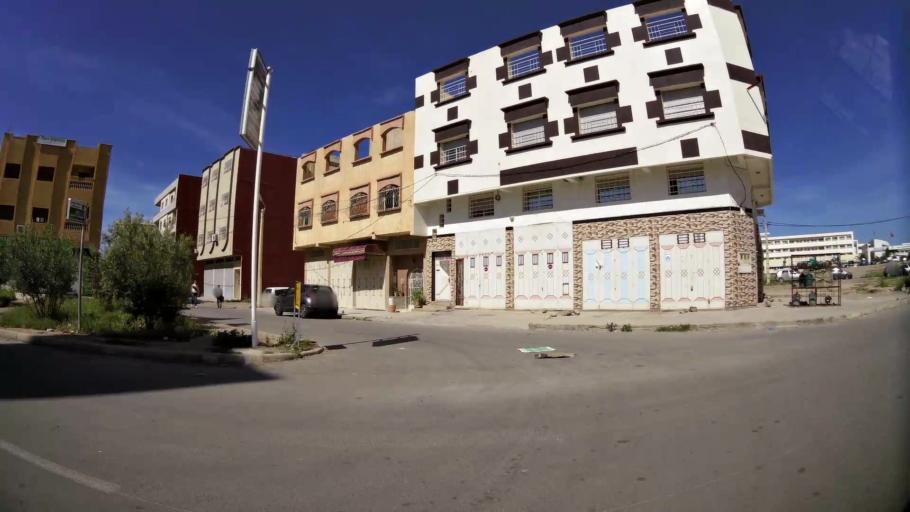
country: MA
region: Oriental
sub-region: Oujda-Angad
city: Oujda
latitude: 34.6568
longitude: -1.9142
